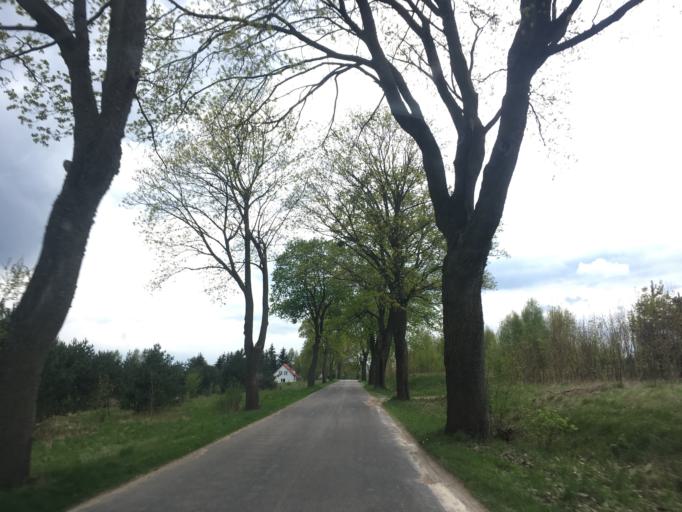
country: PL
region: Warmian-Masurian Voivodeship
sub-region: Powiat nidzicki
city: Kozlowo
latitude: 53.4126
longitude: 20.2682
